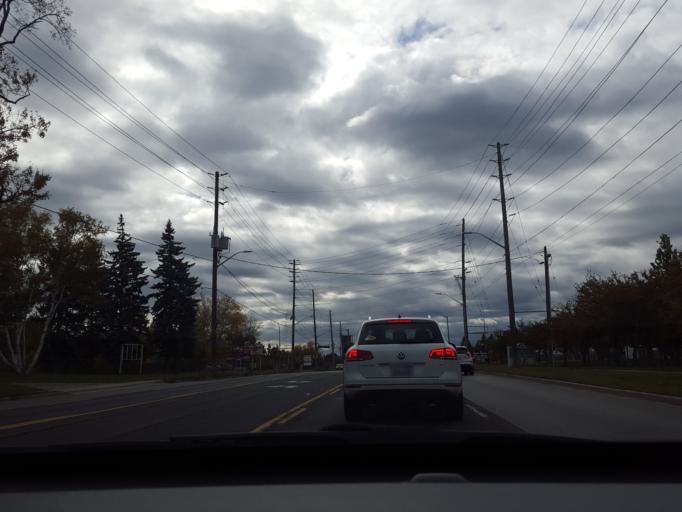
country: CA
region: Ontario
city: Markham
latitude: 43.8424
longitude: -79.3047
